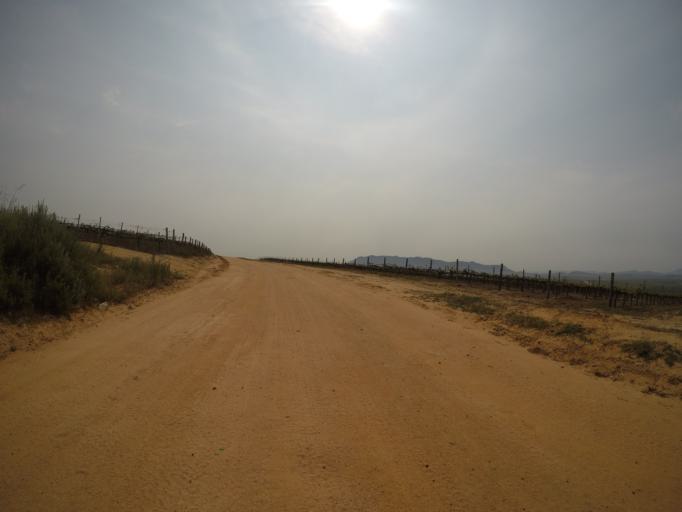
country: ZA
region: Western Cape
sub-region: West Coast District Municipality
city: Malmesbury
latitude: -33.4475
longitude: 18.7471
